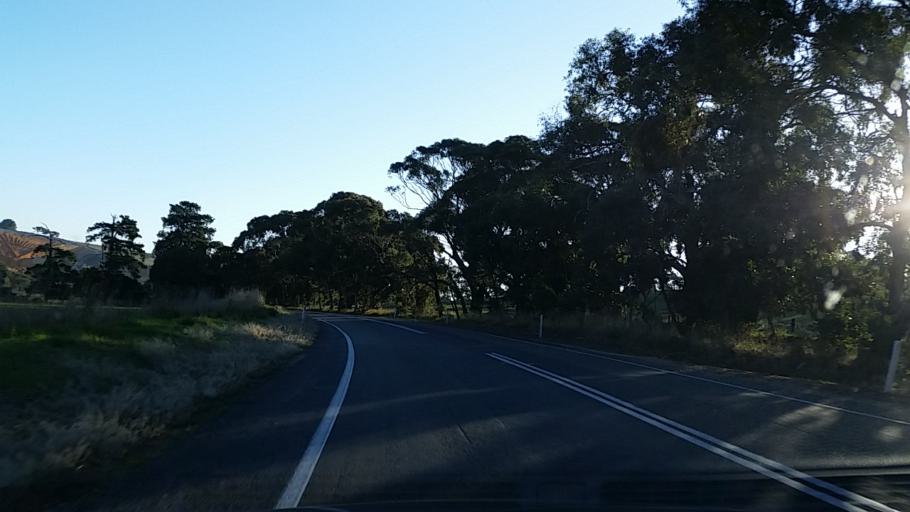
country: AU
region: South Australia
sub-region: Alexandrina
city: Goolwa
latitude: -35.3904
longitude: 138.7569
